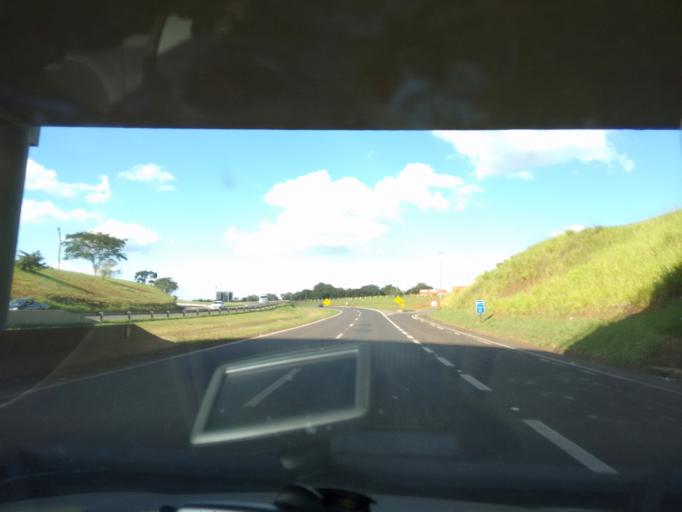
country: BR
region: Sao Paulo
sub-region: Araraquara
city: Araraquara
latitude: -21.8130
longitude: -48.1581
